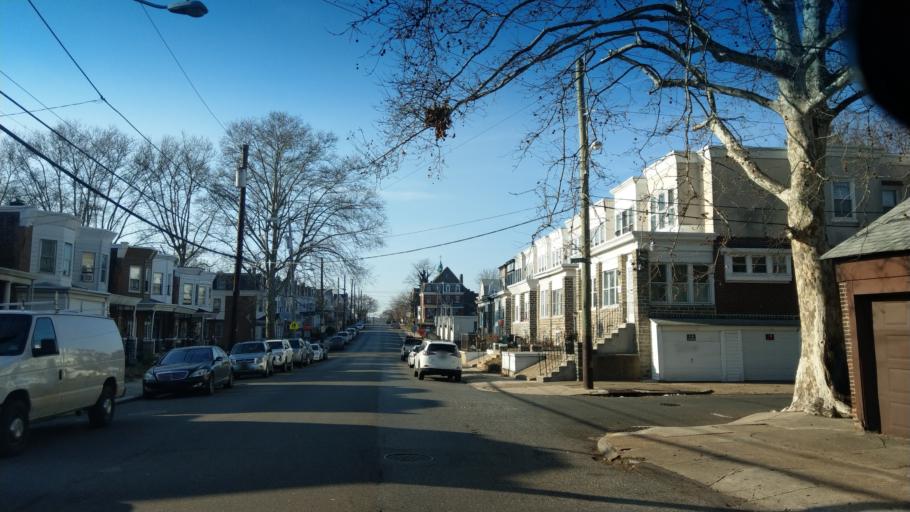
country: US
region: Pennsylvania
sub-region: Montgomery County
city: Rockledge
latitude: 40.0304
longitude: -75.1195
